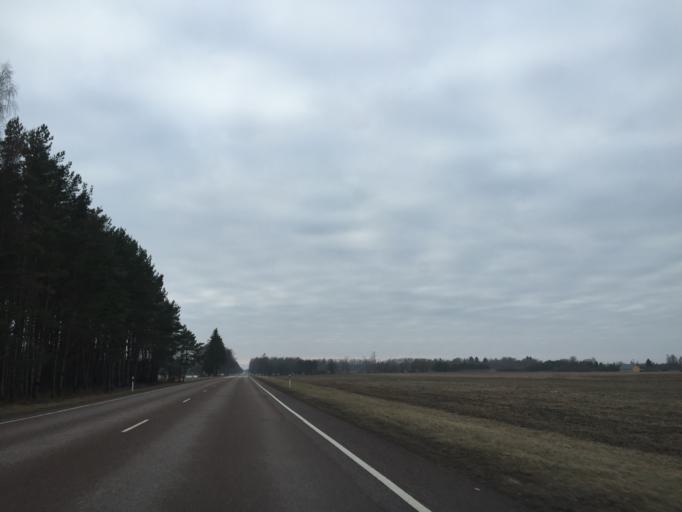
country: EE
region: Saare
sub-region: Orissaare vald
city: Orissaare
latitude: 58.5279
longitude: 23.0173
